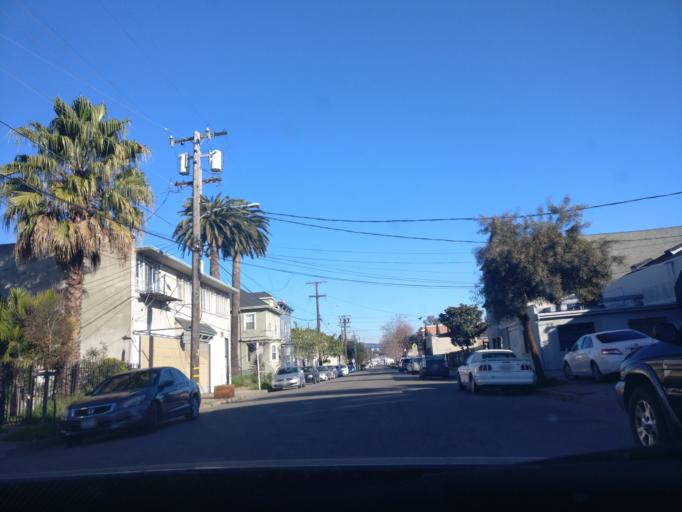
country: US
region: California
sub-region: Alameda County
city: Emeryville
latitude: 37.8194
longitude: -122.2754
